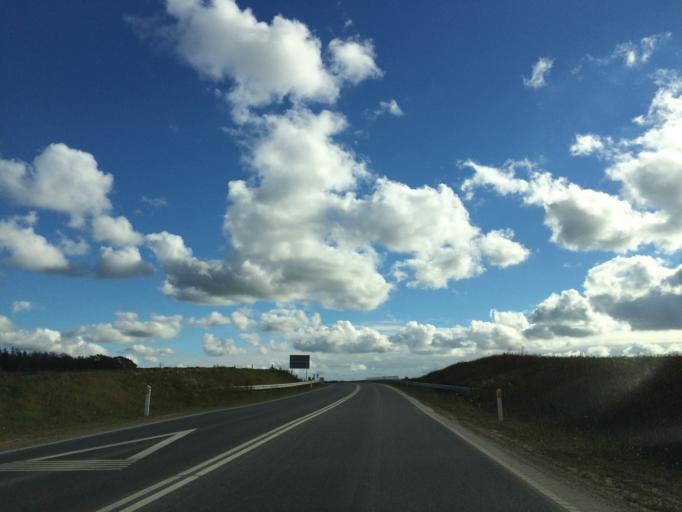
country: DK
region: Central Jutland
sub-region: Skanderborg Kommune
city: Ry
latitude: 56.1475
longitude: 9.7949
